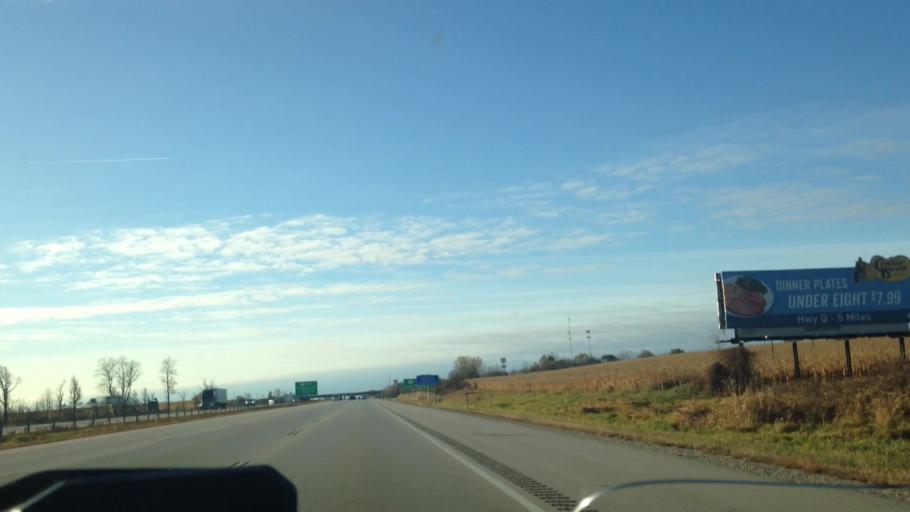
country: US
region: Wisconsin
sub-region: Washington County
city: Richfield
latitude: 43.2585
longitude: -88.1821
